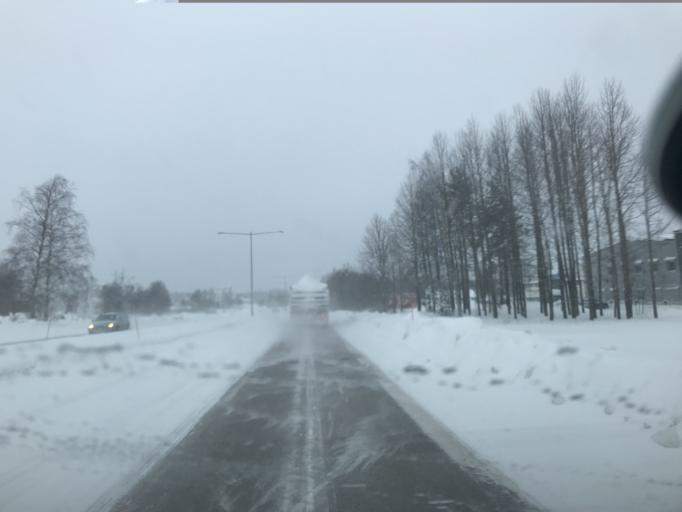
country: SE
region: Norrbotten
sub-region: Lulea Kommun
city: Lulea
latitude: 65.6100
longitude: 22.1365
